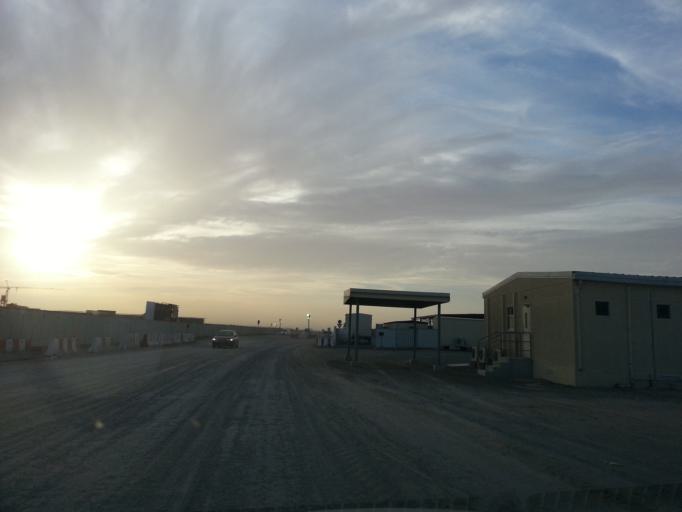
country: AE
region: Abu Dhabi
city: Abu Dhabi
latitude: 24.7793
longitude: 54.7307
